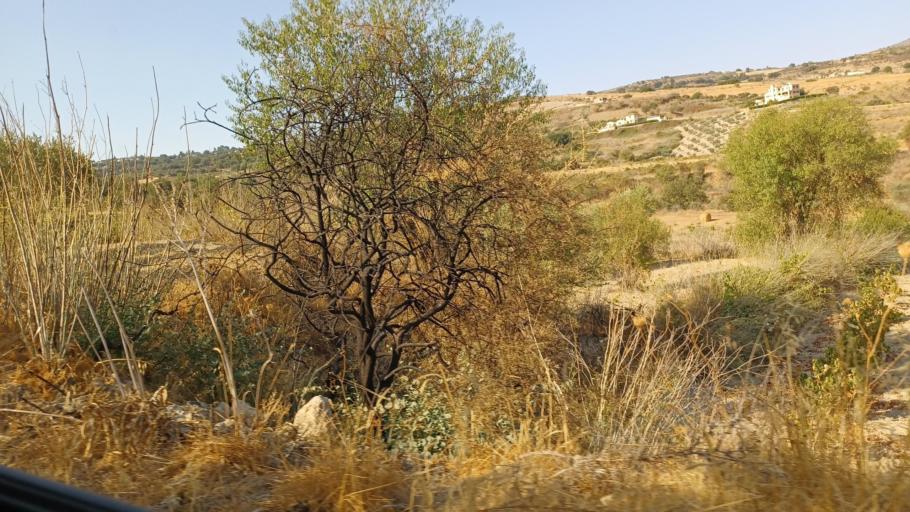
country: CY
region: Pafos
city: Tala
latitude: 34.9084
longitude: 32.4852
